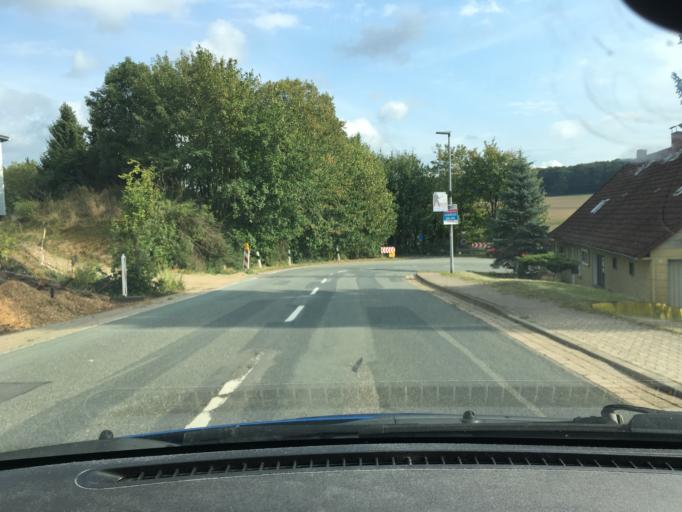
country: DE
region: Lower Saxony
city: Barsinghausen
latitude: 52.2577
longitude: 9.4583
